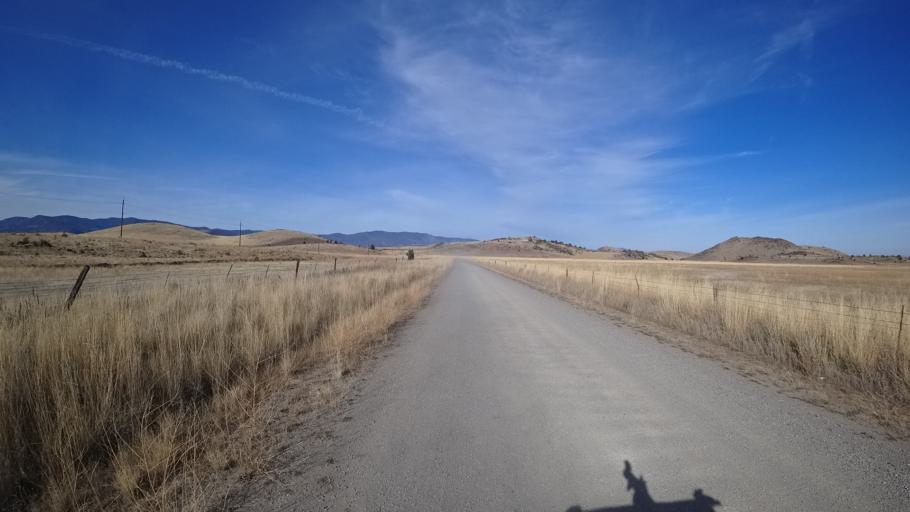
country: US
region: California
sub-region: Siskiyou County
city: Weed
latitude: 41.5087
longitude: -122.4623
